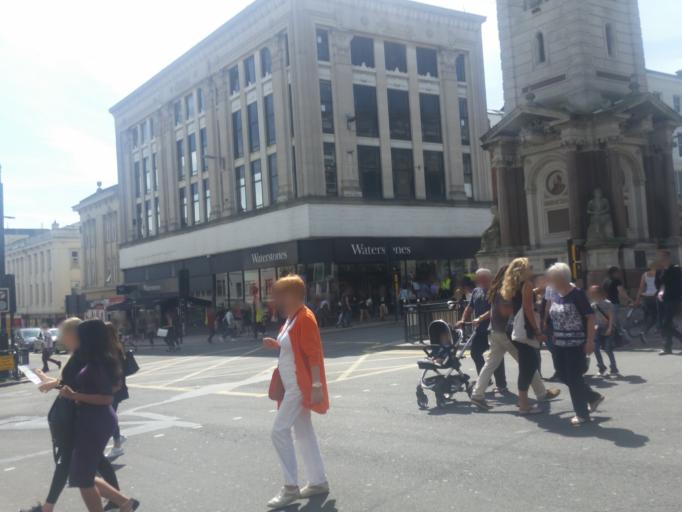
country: GB
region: England
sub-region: Brighton and Hove
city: Brighton
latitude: 50.8238
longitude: -0.1434
